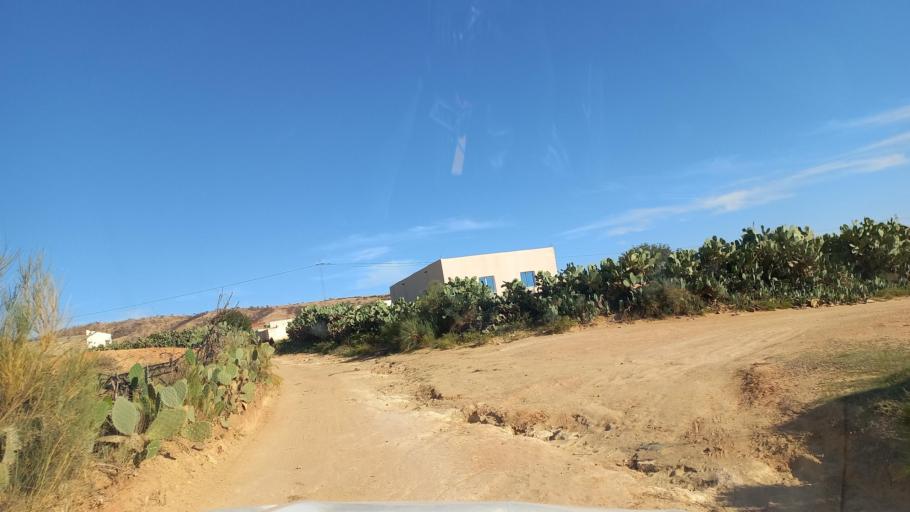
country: TN
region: Al Qasrayn
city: Sbiba
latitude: 35.3291
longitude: 9.1284
